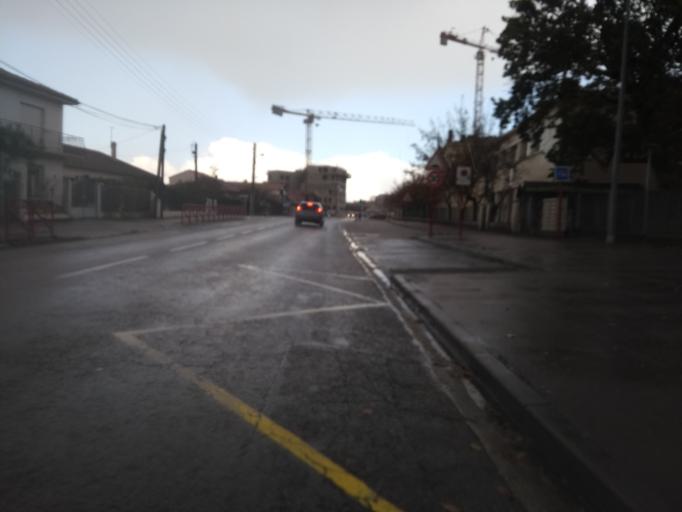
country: FR
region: Aquitaine
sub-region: Departement de la Gironde
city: Villenave-d'Ornon
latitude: 44.7807
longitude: -0.5690
